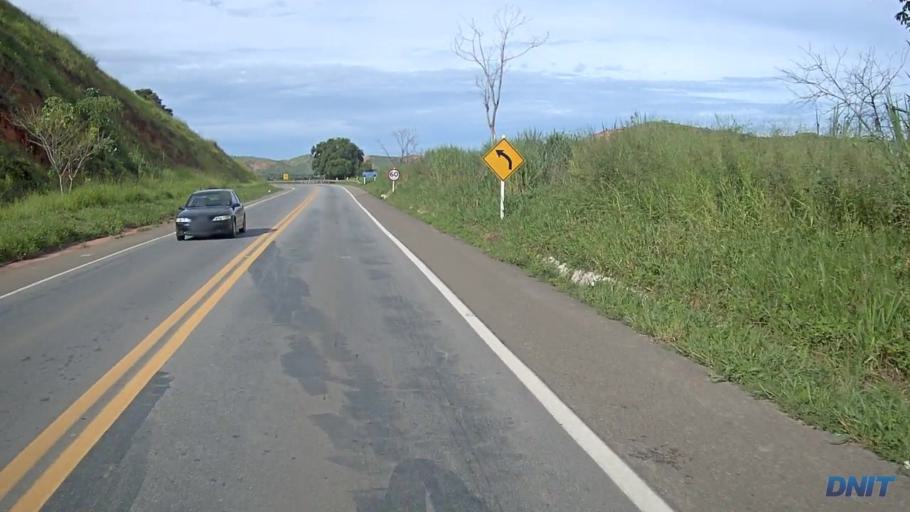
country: BR
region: Minas Gerais
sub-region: Belo Oriente
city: Belo Oriente
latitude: -19.1610
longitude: -42.2398
